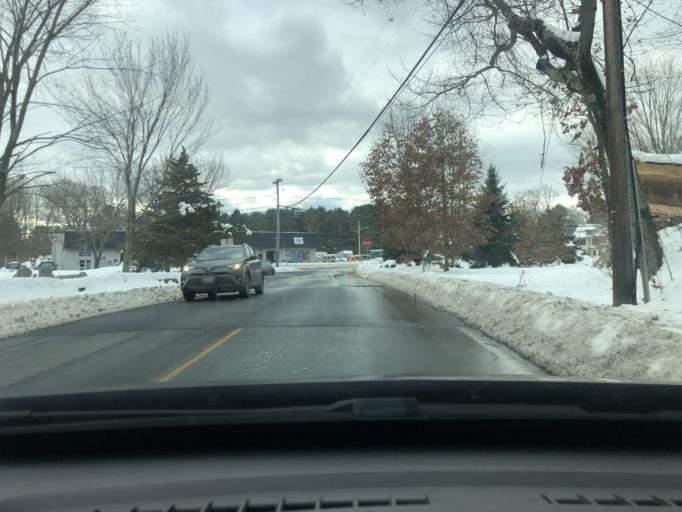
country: US
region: Massachusetts
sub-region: Middlesex County
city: Stow
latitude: 42.4327
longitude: -71.4833
